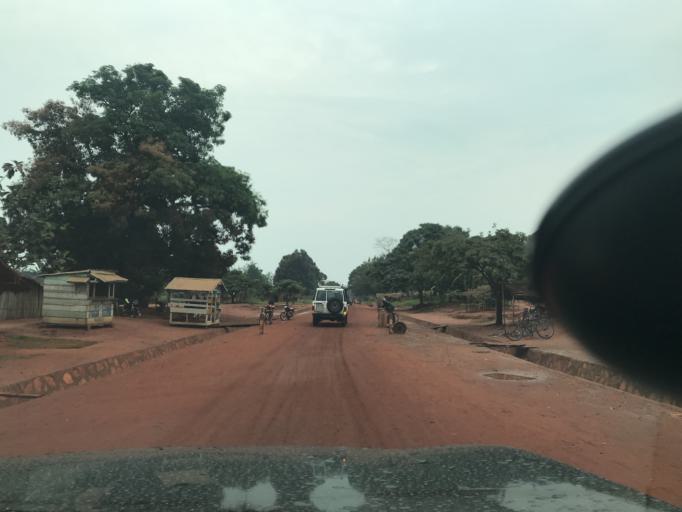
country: CD
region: Equateur
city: Gemena
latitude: 3.2229
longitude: 19.7764
